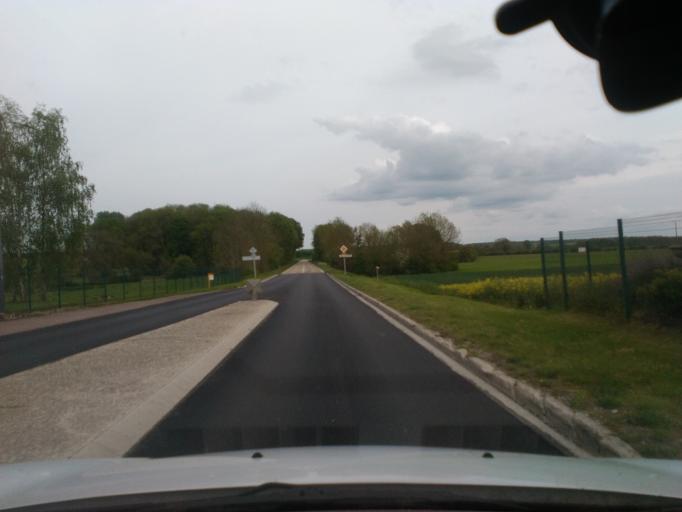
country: FR
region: Champagne-Ardenne
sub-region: Departement de la Haute-Marne
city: Lavilleneuve-au-Roi
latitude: 48.1816
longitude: 4.9821
